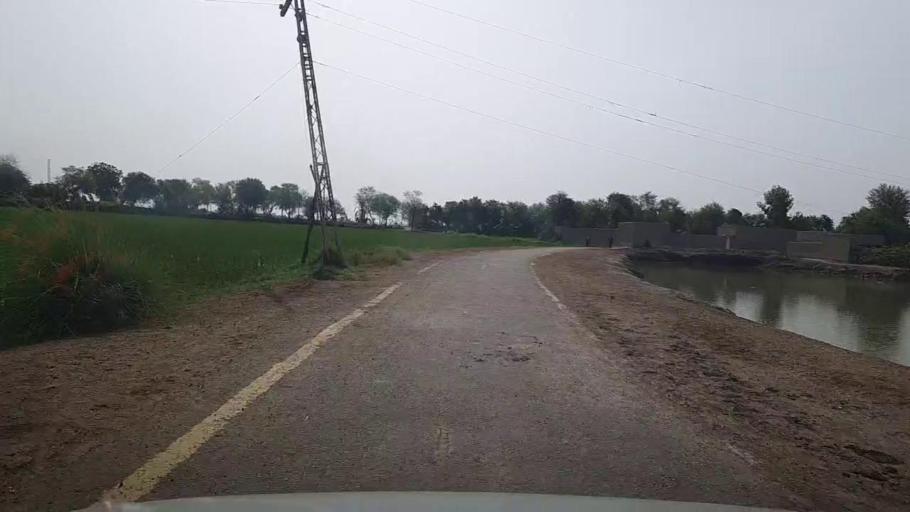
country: PK
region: Sindh
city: Sita Road
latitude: 27.0990
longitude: 67.8243
